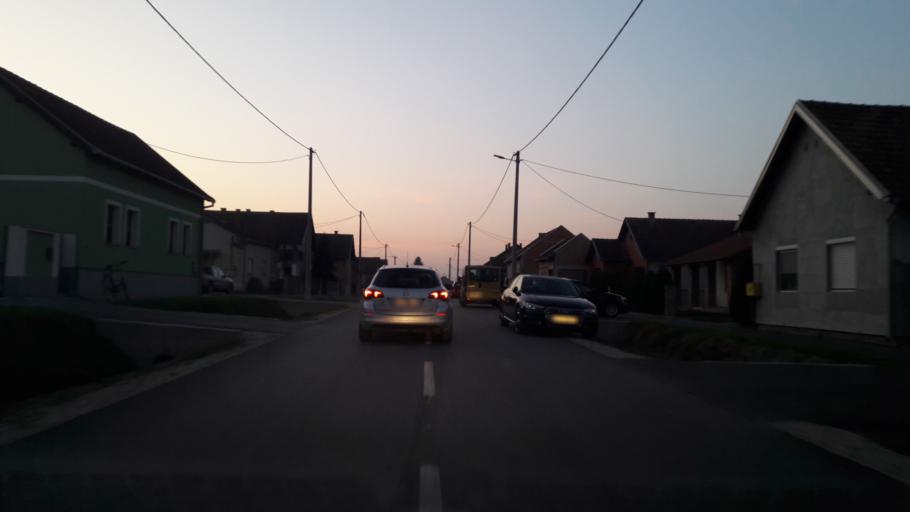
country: HR
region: Vukovarsko-Srijemska
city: Nijemci
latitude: 45.1413
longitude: 19.0350
